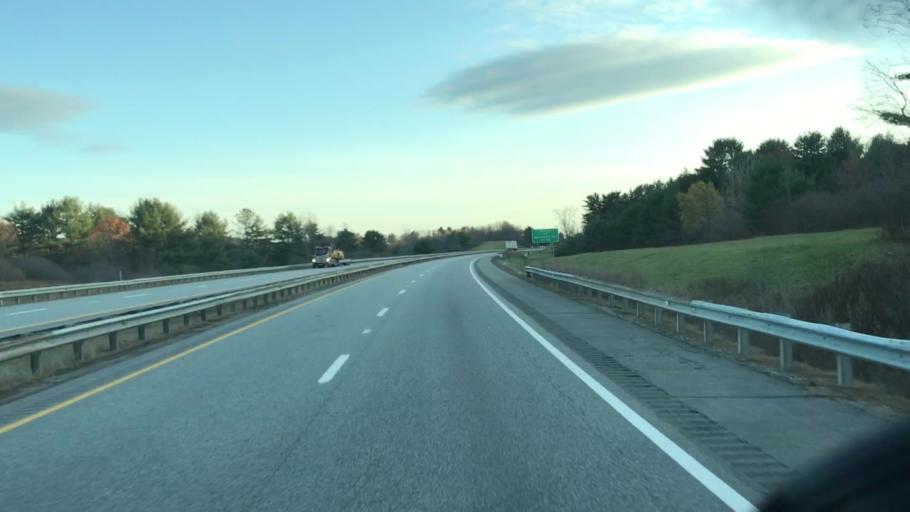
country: US
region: Maine
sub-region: Cumberland County
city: Cumberland Center
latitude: 43.7544
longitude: -70.3046
